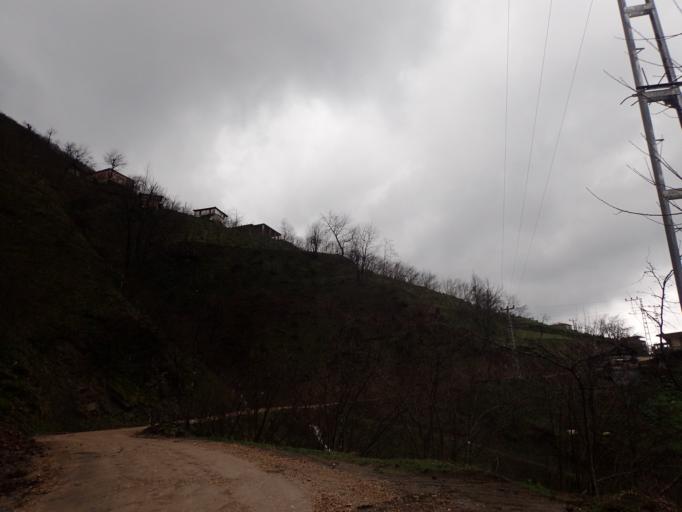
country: TR
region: Ordu
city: Camas
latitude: 40.8696
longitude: 37.5047
